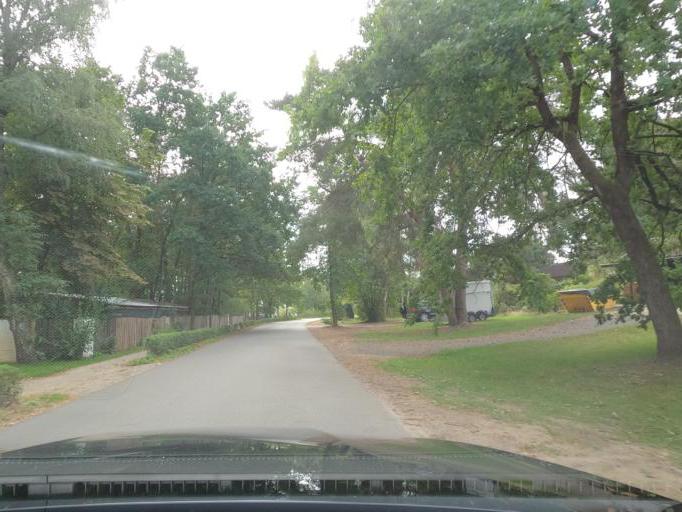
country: DE
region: Lower Saxony
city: Burgdorf
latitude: 52.5060
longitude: 9.9479
